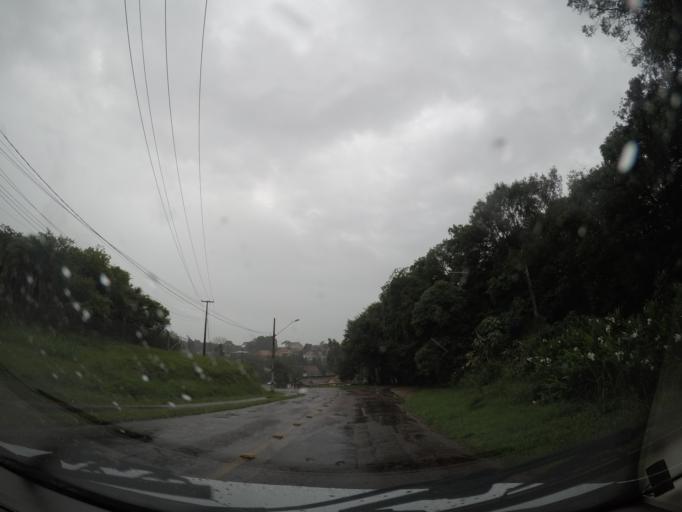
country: BR
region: Parana
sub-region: Curitiba
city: Curitiba
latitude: -25.4555
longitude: -49.3720
